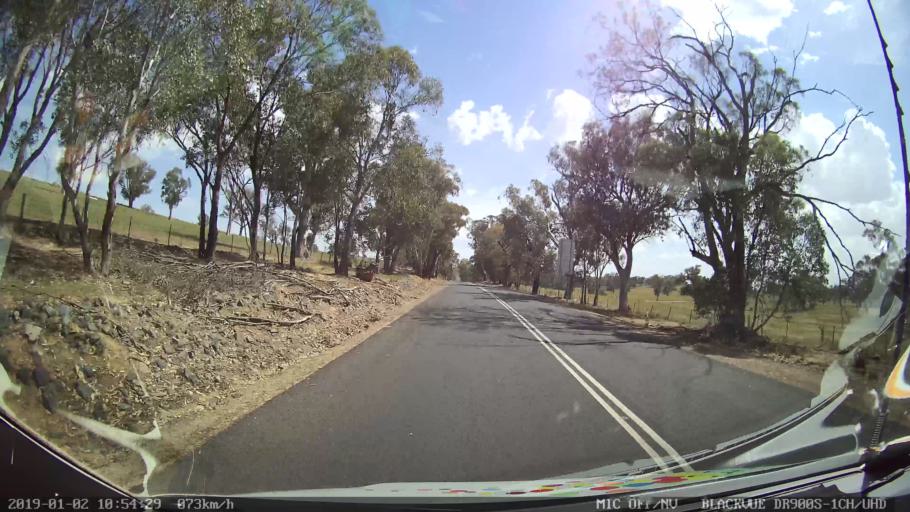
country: AU
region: New South Wales
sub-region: Cootamundra
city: Cootamundra
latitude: -34.6692
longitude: 148.2733
